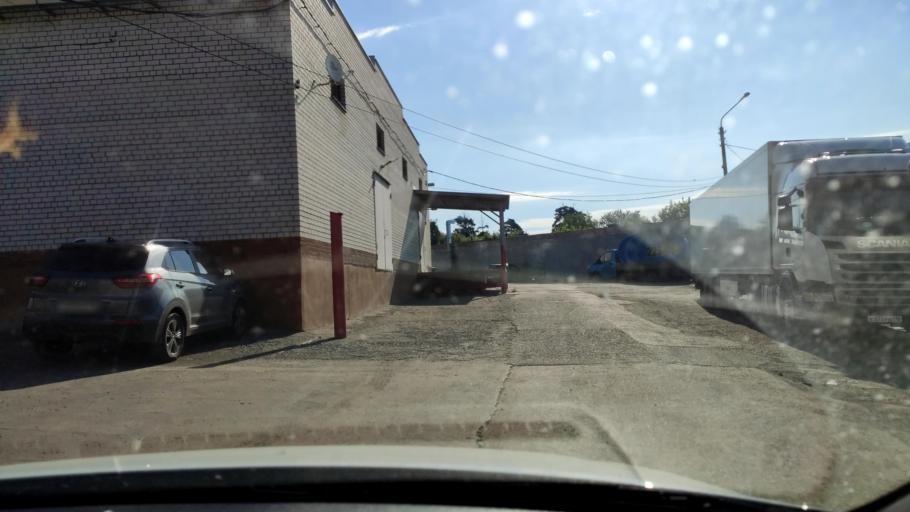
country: RU
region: Tatarstan
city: Staroye Arakchino
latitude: 55.8412
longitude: 49.0438
